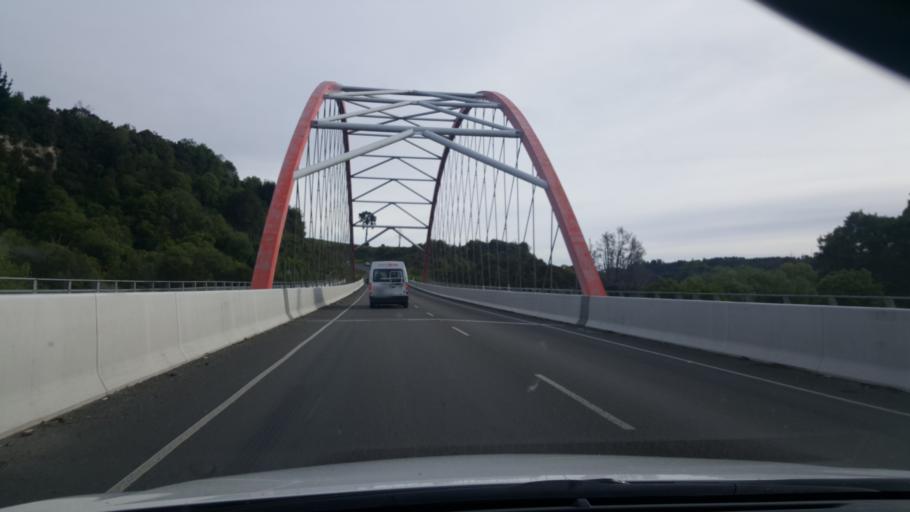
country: NZ
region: Waikato
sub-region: Taupo District
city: Taupo
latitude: -38.6328
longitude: 176.0978
